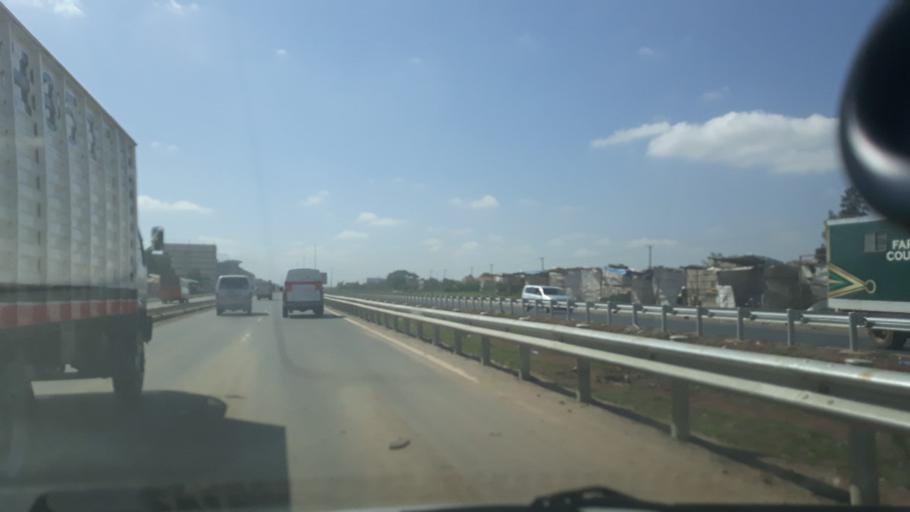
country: KE
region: Nairobi Area
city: Pumwani
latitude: -1.2856
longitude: 36.8841
